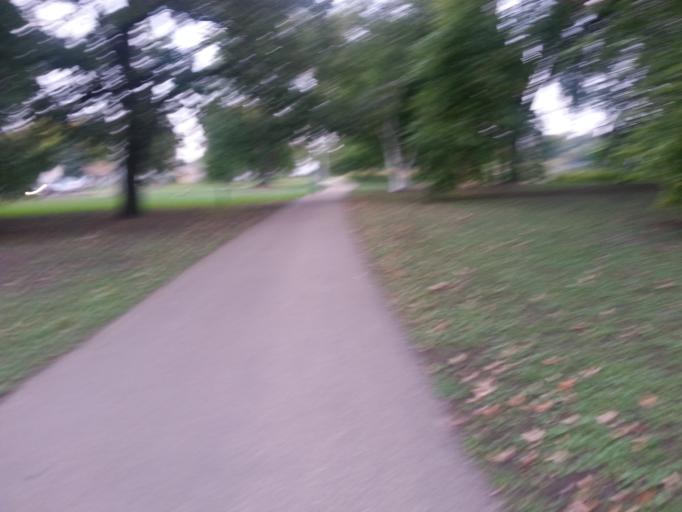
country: US
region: Minnesota
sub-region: Olmsted County
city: Rochester
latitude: 44.0318
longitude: -92.4582
